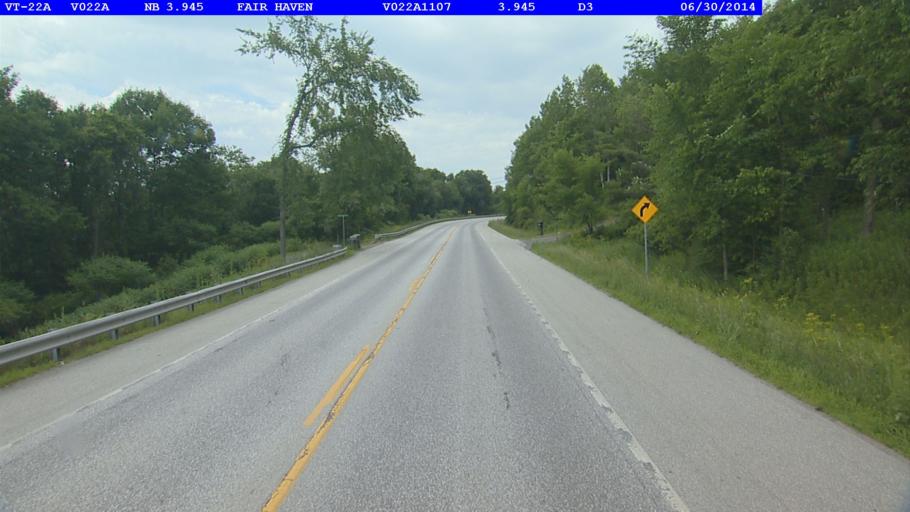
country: US
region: Vermont
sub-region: Rutland County
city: Fair Haven
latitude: 43.6213
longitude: -73.2973
